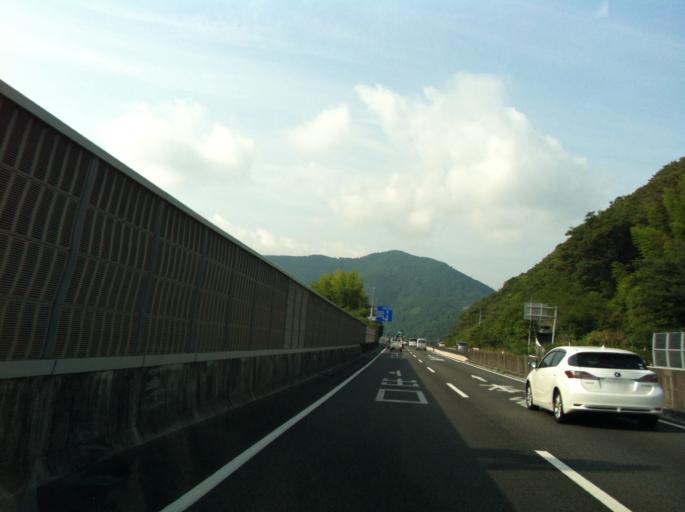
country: JP
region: Shizuoka
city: Shizuoka-shi
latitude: 34.9818
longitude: 138.3504
